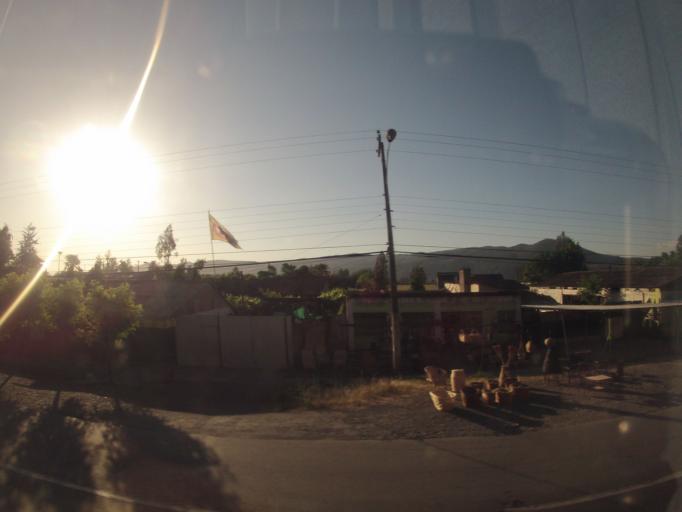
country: CL
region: O'Higgins
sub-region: Provincia de Colchagua
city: Chimbarongo
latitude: -34.7123
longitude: -71.0295
